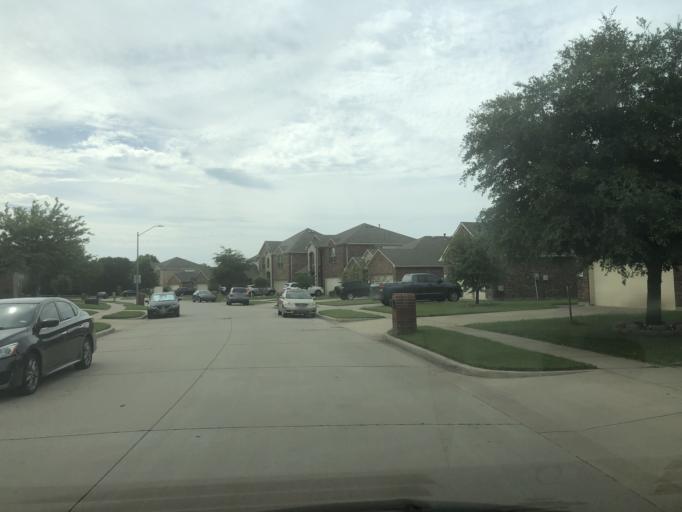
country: US
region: Texas
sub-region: Dallas County
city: Irving
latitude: 32.7951
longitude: -96.9879
